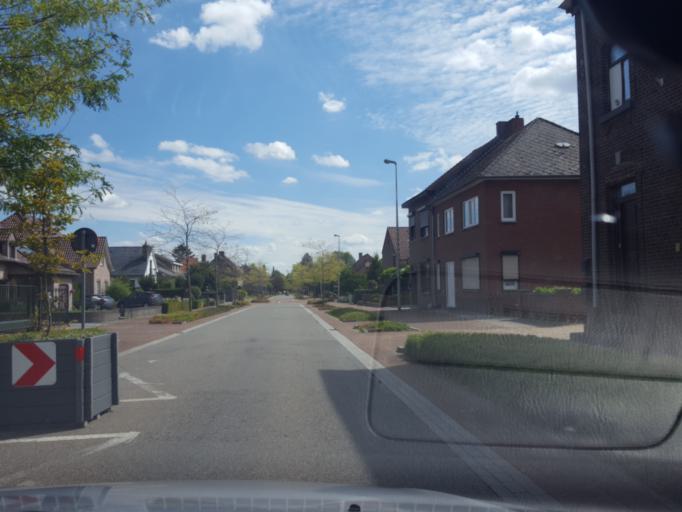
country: BE
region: Flanders
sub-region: Provincie Limburg
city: Maasmechelen
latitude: 50.9269
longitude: 5.6903
